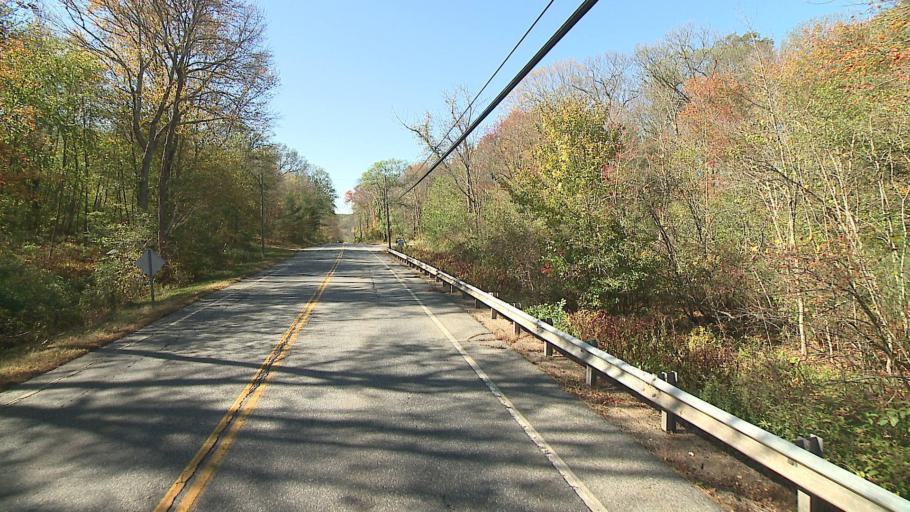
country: US
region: Connecticut
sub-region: Hartford County
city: Terramuggus
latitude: 41.6472
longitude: -72.4291
